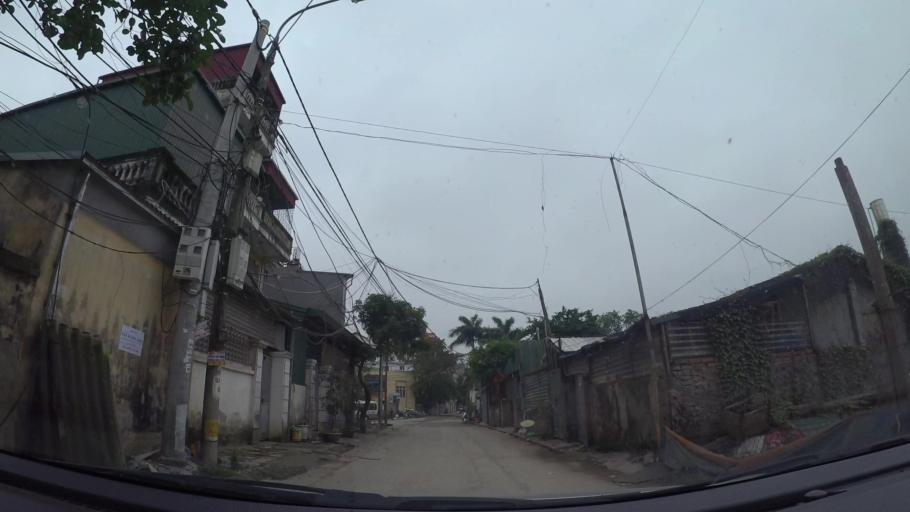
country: VN
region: Ha Noi
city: Tay Ho
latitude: 21.0654
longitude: 105.8371
